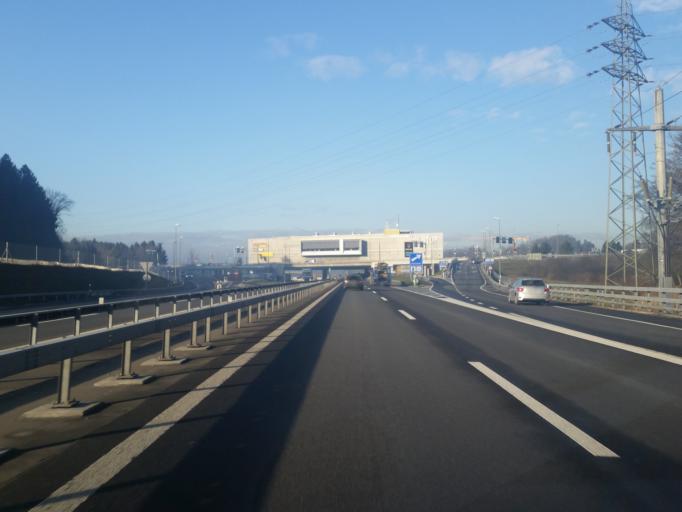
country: CH
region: Zurich
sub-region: Bezirk Affoltern
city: Obfelden / Toussen
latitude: 47.2687
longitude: 8.4393
